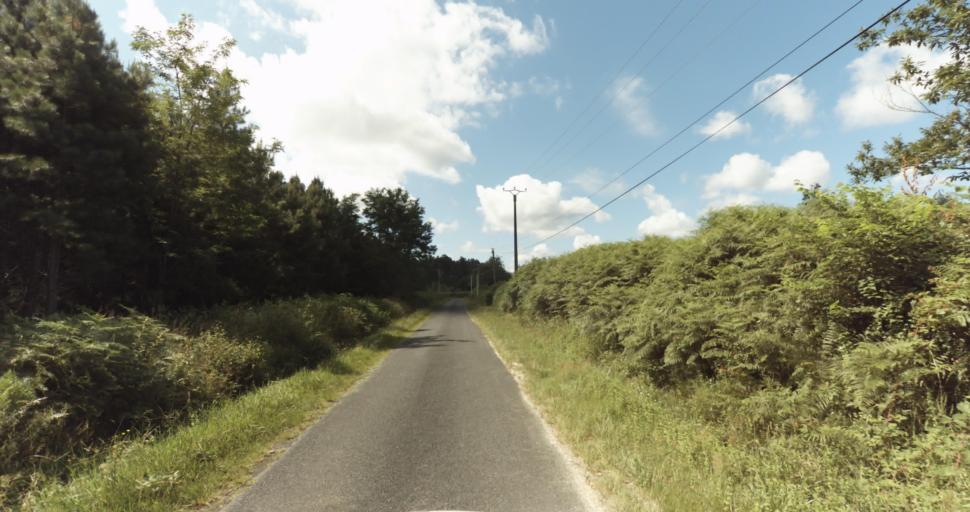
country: FR
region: Aquitaine
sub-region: Departement de la Gironde
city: Bazas
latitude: 44.4535
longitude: -0.2169
